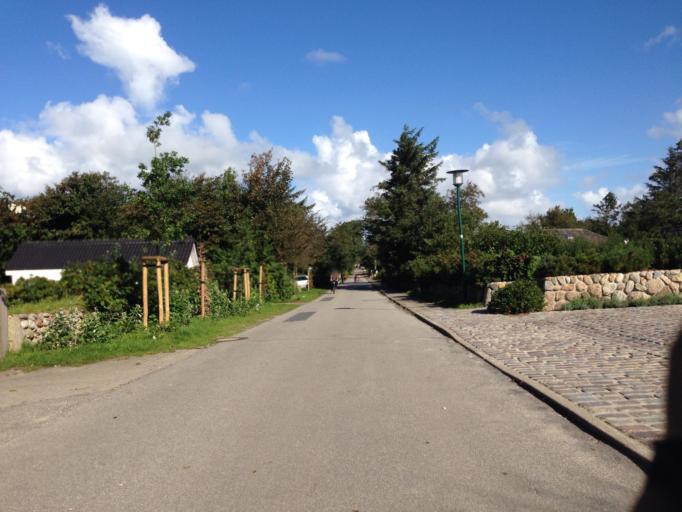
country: DE
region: Schleswig-Holstein
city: Borgsum
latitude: 54.6846
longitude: 8.4680
